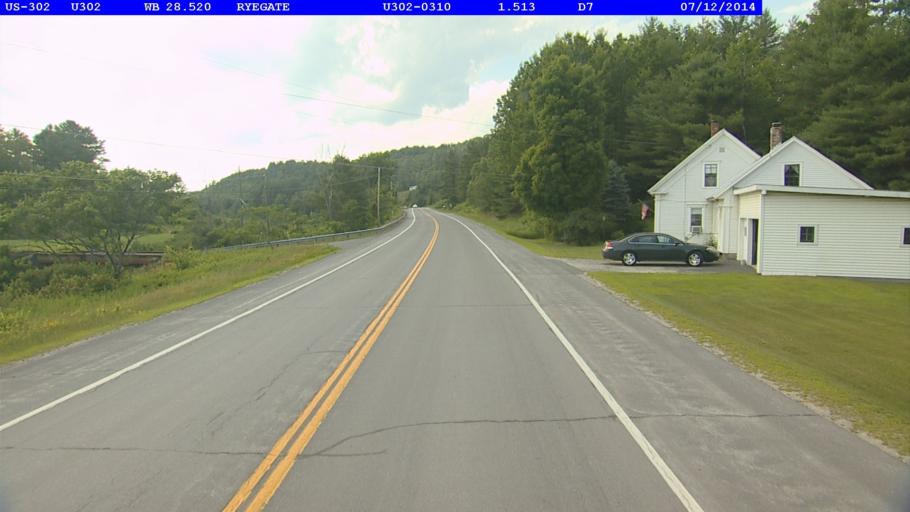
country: US
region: New Hampshire
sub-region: Grafton County
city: Woodsville
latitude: 44.1928
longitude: -72.1475
